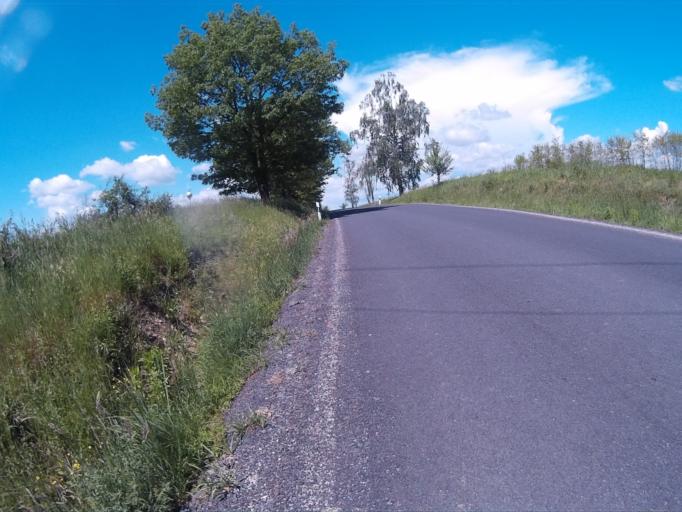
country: HU
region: Vas
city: Kormend
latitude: 46.9688
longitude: 16.5709
